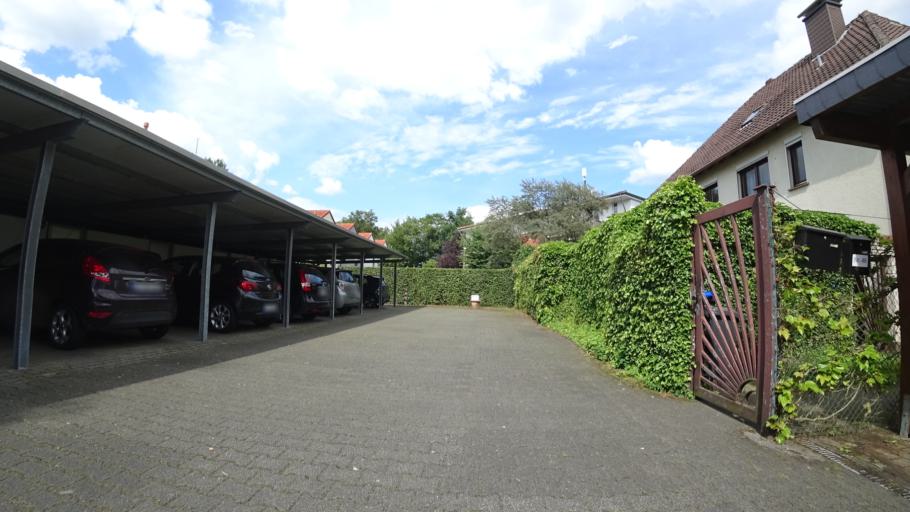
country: DE
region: North Rhine-Westphalia
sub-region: Regierungsbezirk Detmold
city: Guetersloh
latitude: 51.9191
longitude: 8.3847
